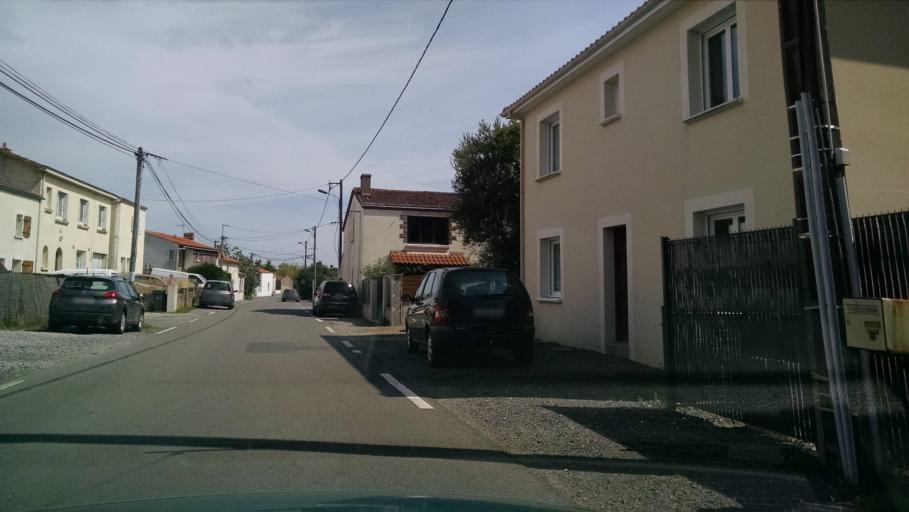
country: FR
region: Pays de la Loire
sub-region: Departement de la Loire-Atlantique
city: Clisson
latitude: 47.1064
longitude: -1.2733
